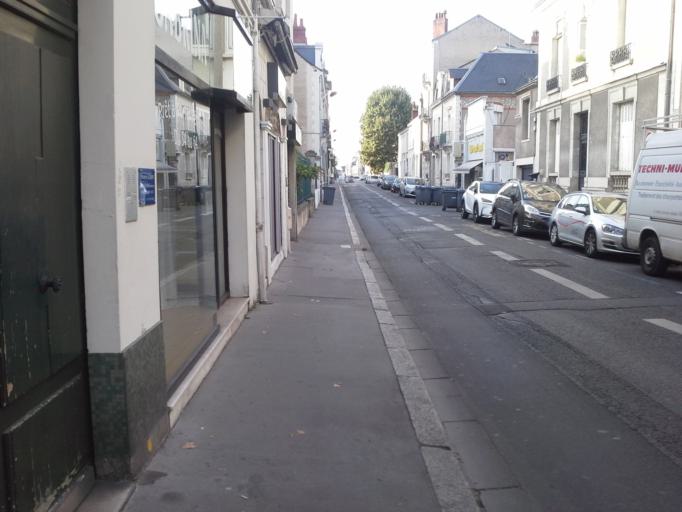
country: FR
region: Centre
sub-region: Departement d'Indre-et-Loire
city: Tours
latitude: 47.3884
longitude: 0.6915
